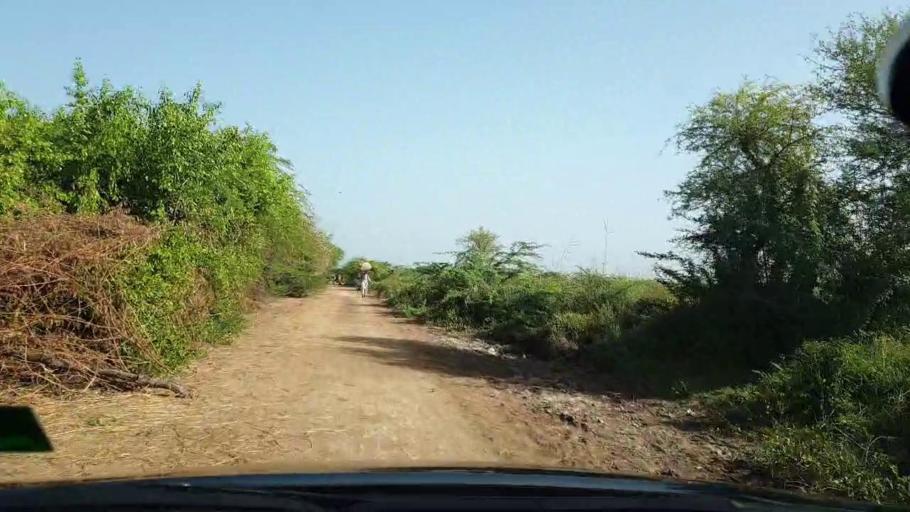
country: PK
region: Sindh
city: Tando Bago
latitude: 24.6626
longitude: 69.0430
